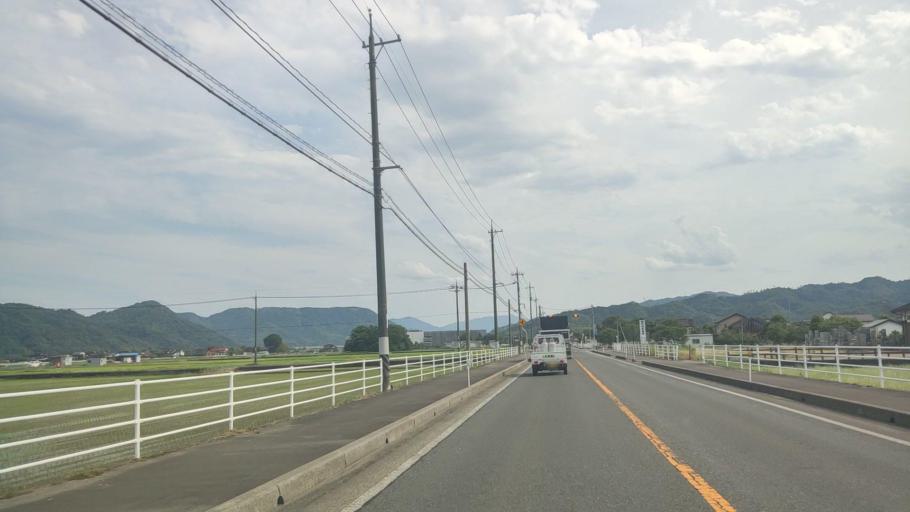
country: JP
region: Tottori
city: Tottori
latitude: 35.4596
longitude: 134.2037
